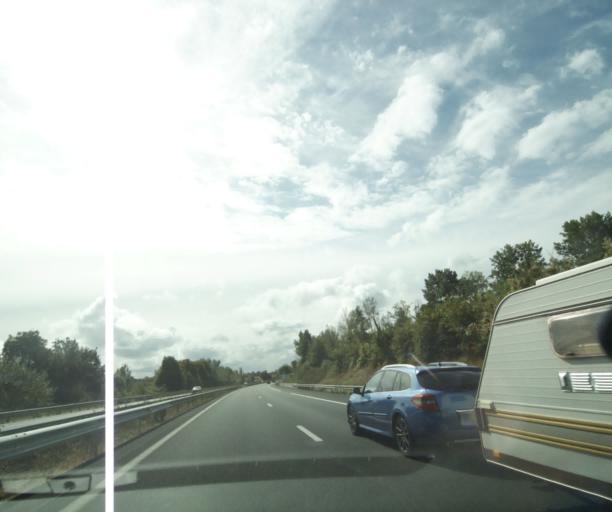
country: FR
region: Poitou-Charentes
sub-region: Departement de la Charente-Maritime
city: Pons
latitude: 45.6005
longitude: -0.5903
